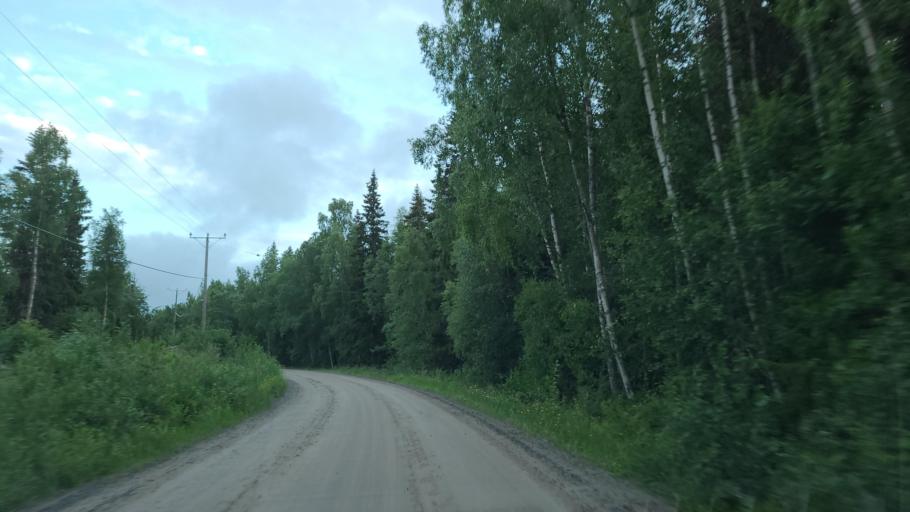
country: FI
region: Ostrobothnia
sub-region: Vaasa
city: Replot
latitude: 63.3066
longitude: 21.1548
